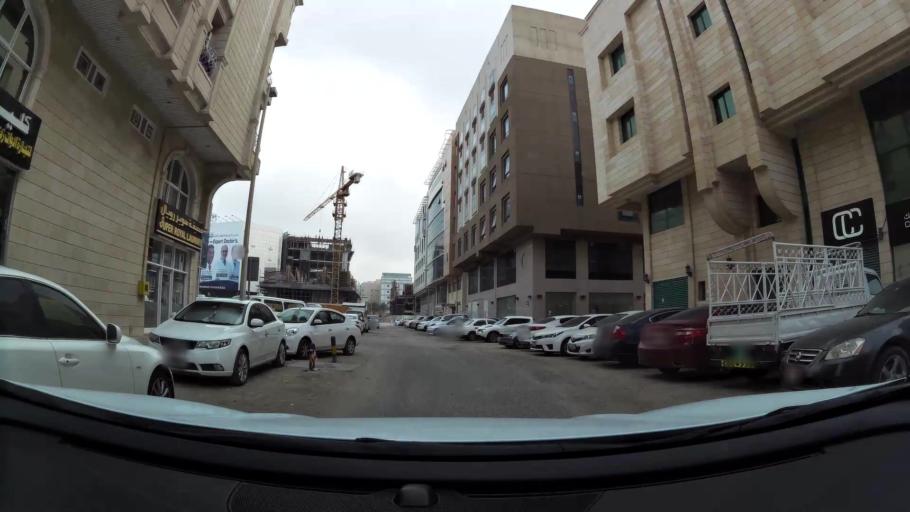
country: AE
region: Abu Dhabi
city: Abu Dhabi
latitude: 24.4761
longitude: 54.3808
